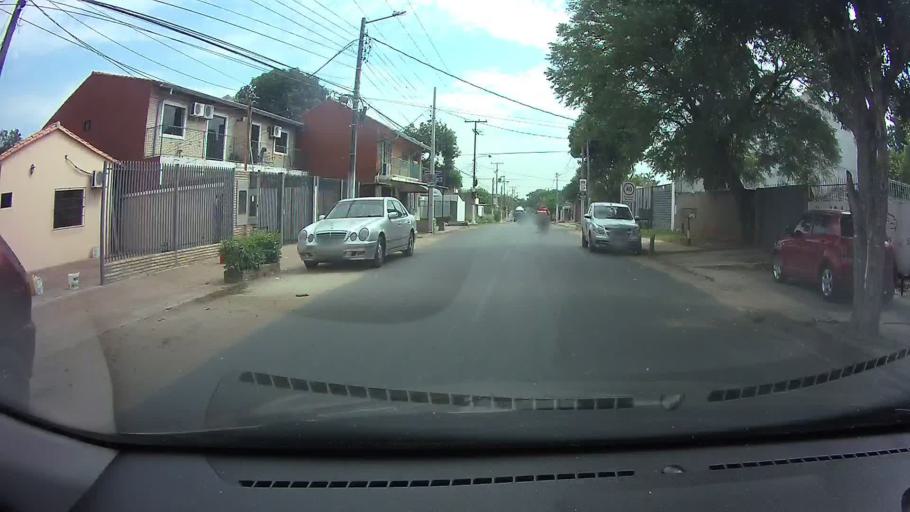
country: PY
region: Central
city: Fernando de la Mora
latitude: -25.3013
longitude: -57.5395
